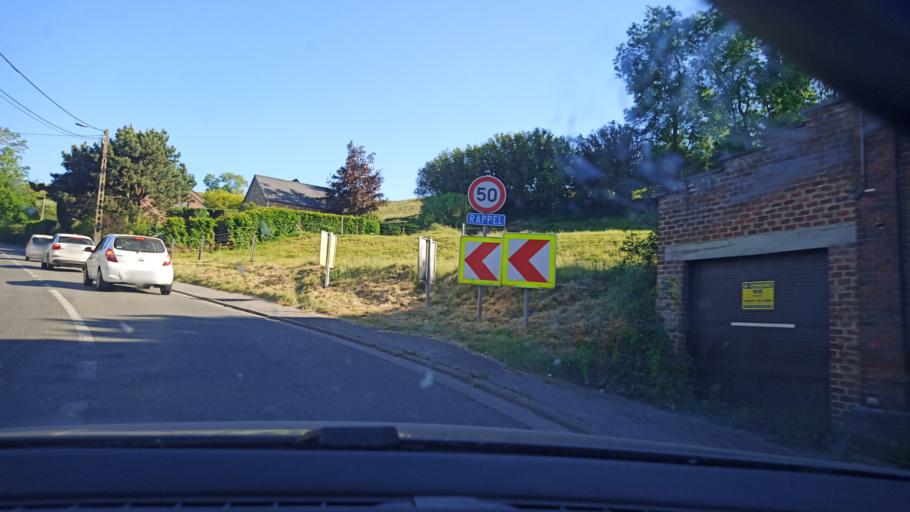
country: BE
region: Wallonia
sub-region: Province du Hainaut
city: Lobbes
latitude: 50.3420
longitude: 4.2631
